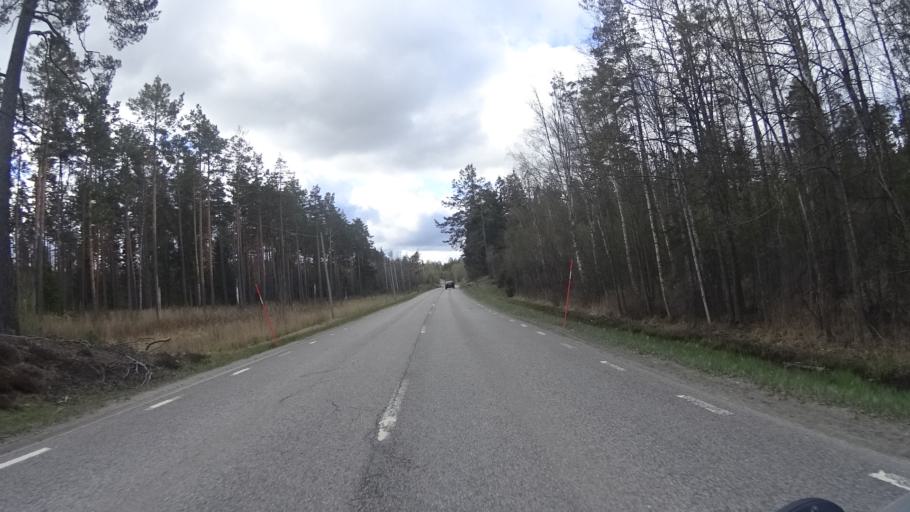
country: SE
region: Stockholm
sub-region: Botkyrka Kommun
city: Tullinge
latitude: 59.1879
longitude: 17.9288
